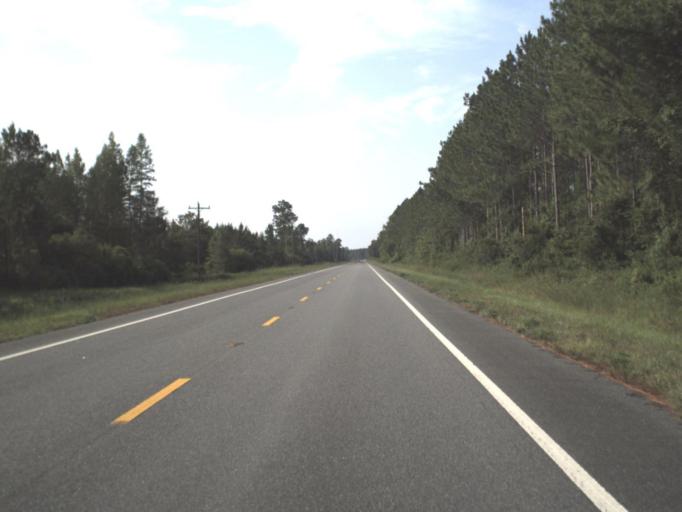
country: US
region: Florida
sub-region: Taylor County
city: Perry
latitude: 30.2291
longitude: -83.6168
